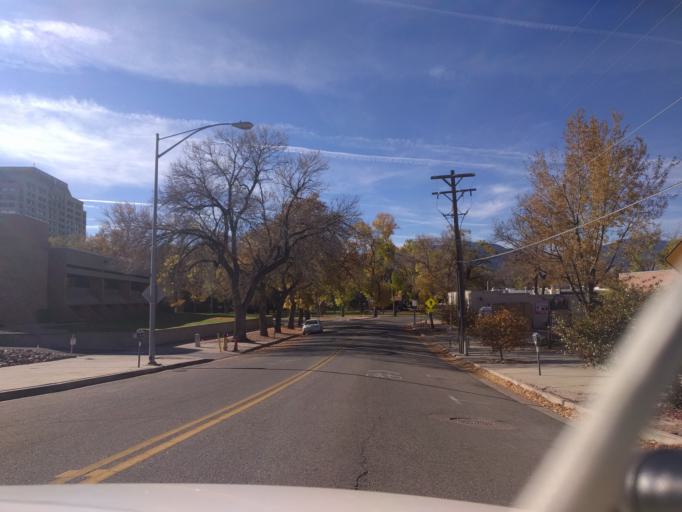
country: US
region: Colorado
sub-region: El Paso County
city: Colorado Springs
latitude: 38.8356
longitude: -104.8277
